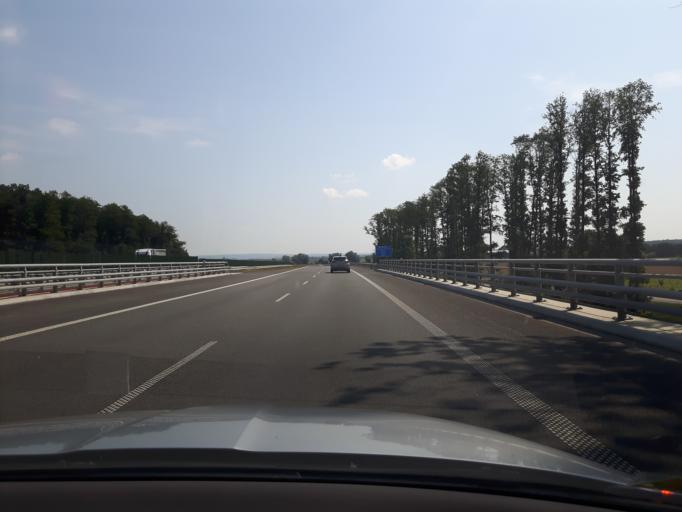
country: PL
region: Warmian-Masurian Voivodeship
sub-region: Powiat elblaski
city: Gronowo Elblaskie
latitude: 54.1647
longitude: 19.2464
